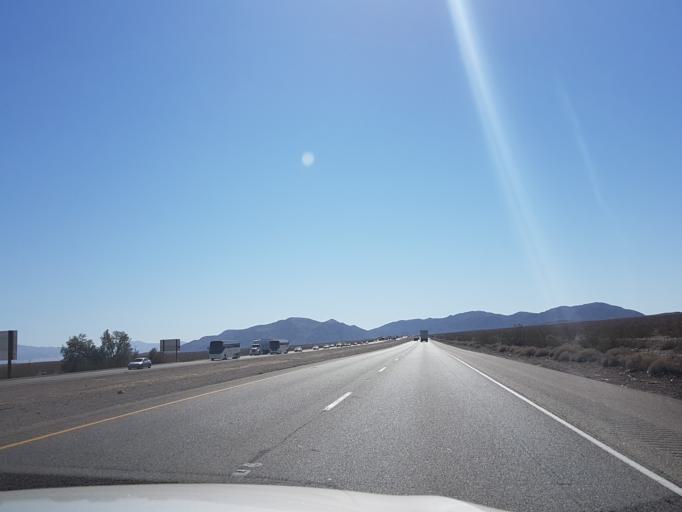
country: US
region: California
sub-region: San Bernardino County
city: Fort Irwin
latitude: 35.2410
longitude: -116.0971
